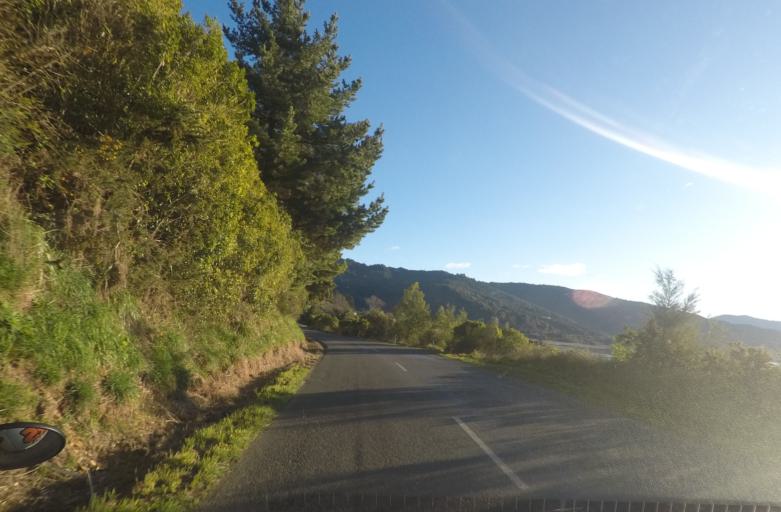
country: NZ
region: Marlborough
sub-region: Marlborough District
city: Picton
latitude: -41.2925
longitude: 173.8370
